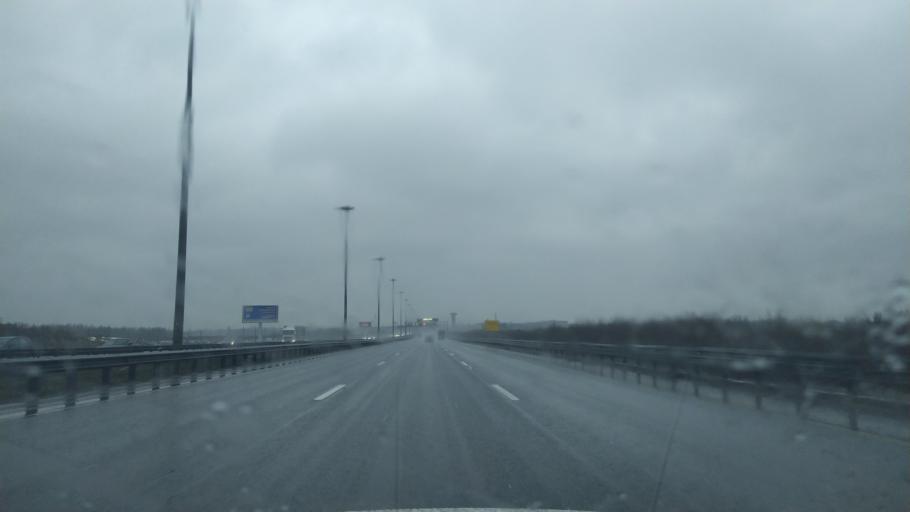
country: RU
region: Leningrad
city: Bugry
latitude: 60.0750
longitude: 30.3815
